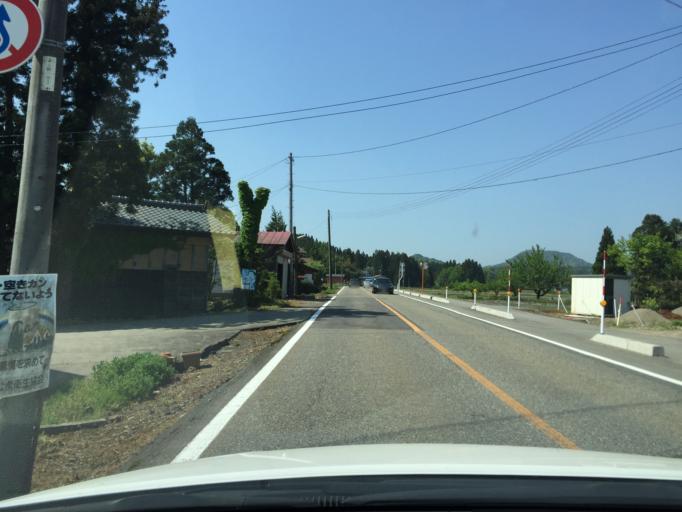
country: JP
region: Niigata
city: Muramatsu
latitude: 37.6713
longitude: 139.1469
